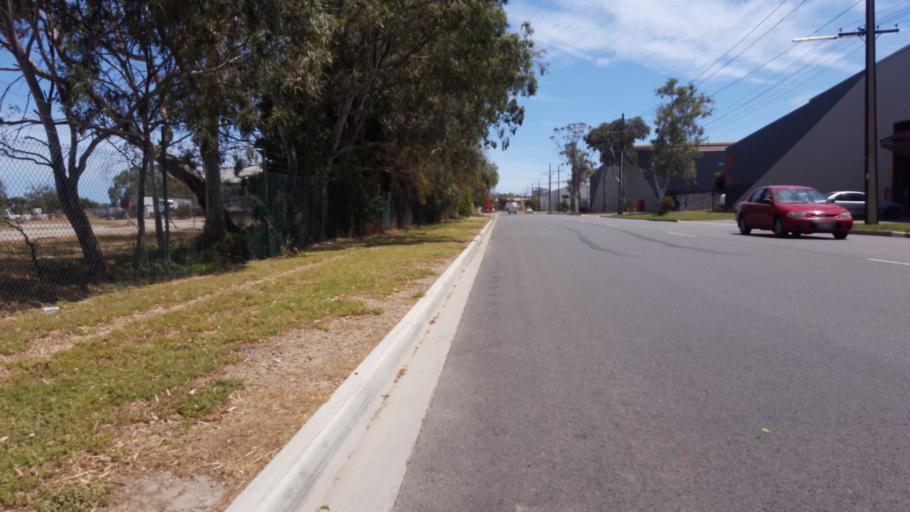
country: AU
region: South Australia
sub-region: Port Adelaide Enfield
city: Alberton
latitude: -34.8437
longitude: 138.5232
